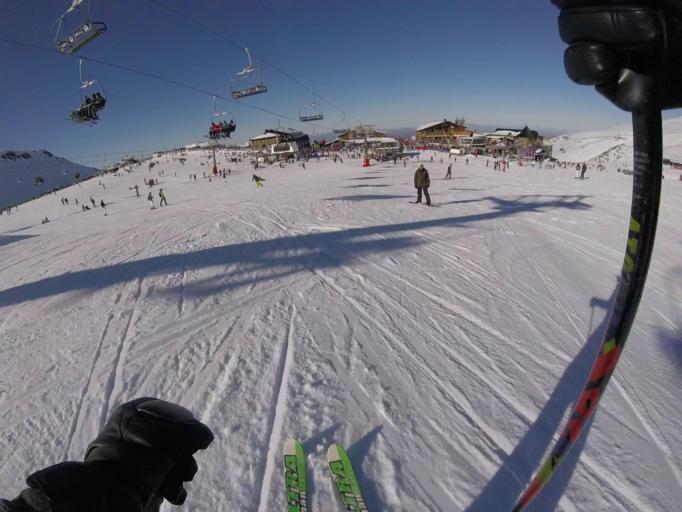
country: ES
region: Andalusia
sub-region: Provincia de Granada
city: Guejar-Sierra
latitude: 37.0699
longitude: -3.3881
